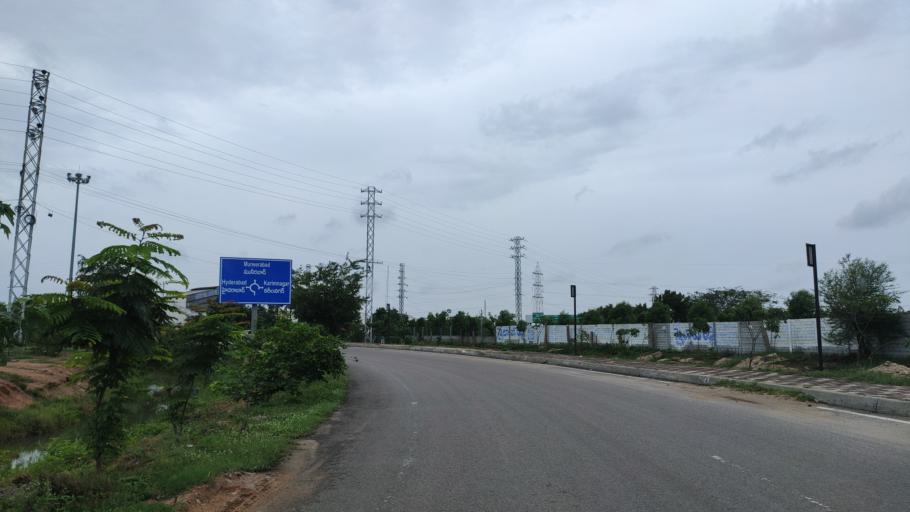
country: IN
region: Telangana
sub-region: Rangareddi
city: Secunderabad
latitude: 17.5792
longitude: 78.5754
